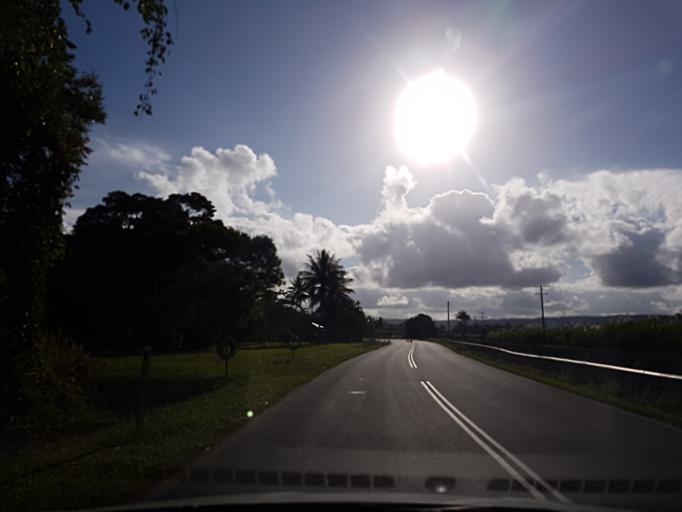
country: AU
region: Queensland
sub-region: Cairns
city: Port Douglas
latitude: -16.3920
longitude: 145.3975
